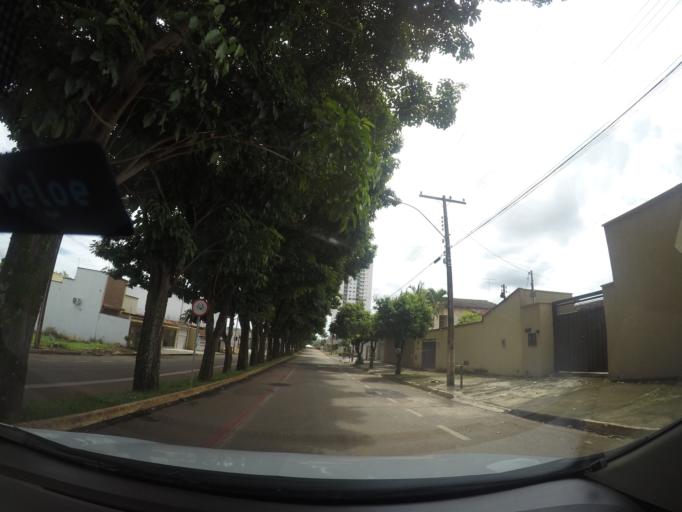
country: BR
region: Goias
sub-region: Inhumas
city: Inhumas
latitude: -16.3685
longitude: -49.5006
